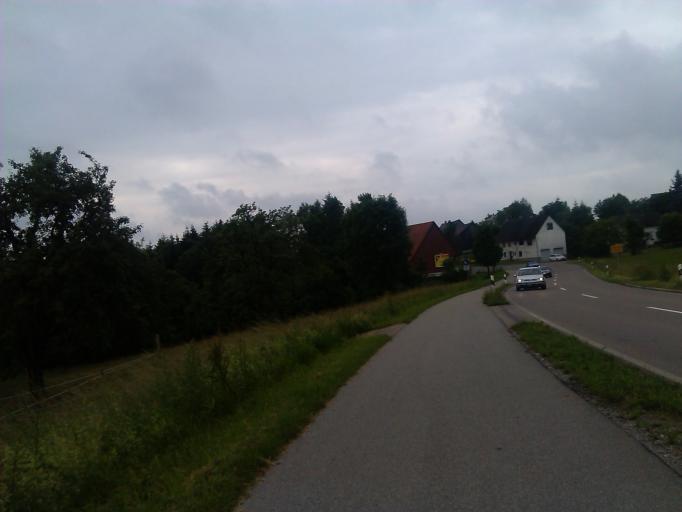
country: DE
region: Baden-Wuerttemberg
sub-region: Regierungsbezirk Stuttgart
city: Mainhardt
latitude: 49.0827
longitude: 9.5310
